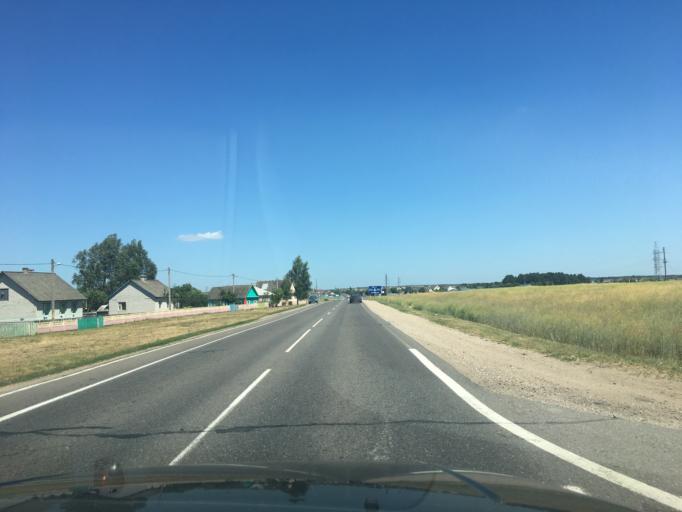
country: BY
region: Grodnenskaya
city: Iwye
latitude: 53.9112
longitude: 25.7626
